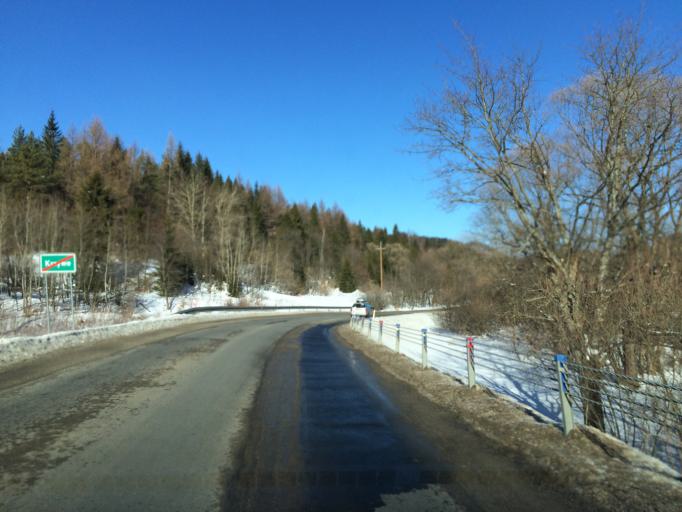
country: PL
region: Subcarpathian Voivodeship
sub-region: Powiat leski
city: Cisna
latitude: 49.2041
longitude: 22.3634
